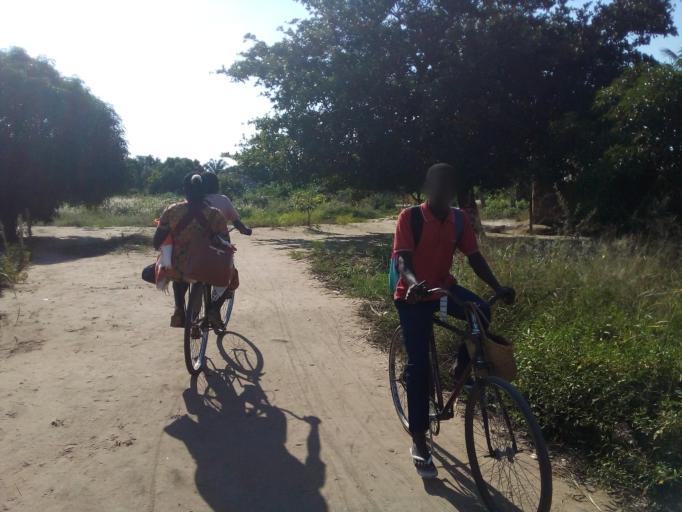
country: MZ
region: Zambezia
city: Quelimane
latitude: -17.5551
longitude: 36.7008
